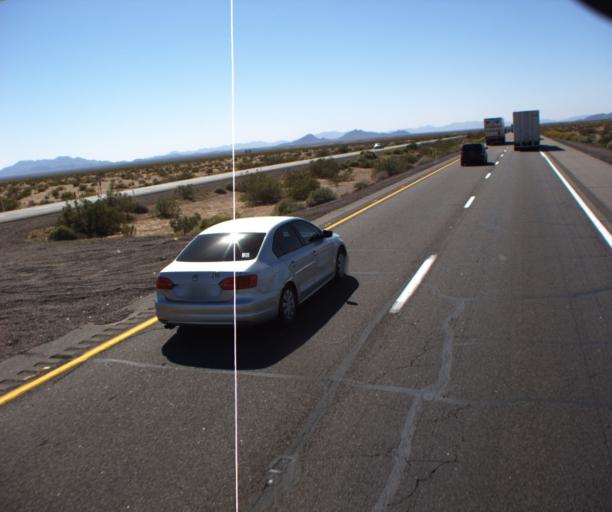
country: US
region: Arizona
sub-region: Yuma County
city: Wellton
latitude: 32.7142
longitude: -113.8185
